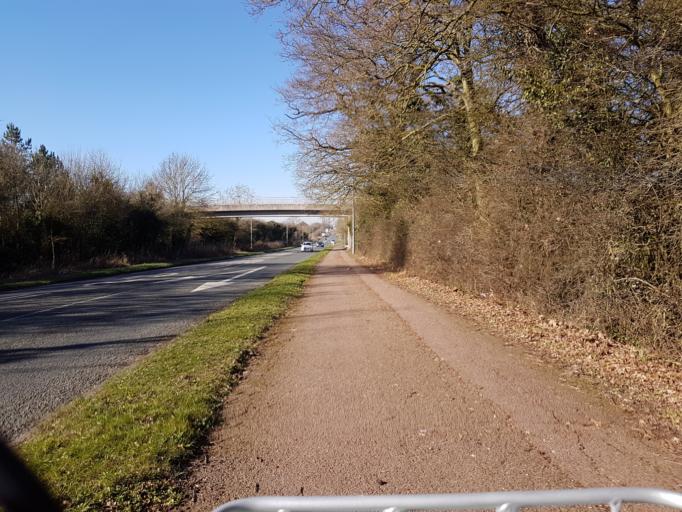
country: GB
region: England
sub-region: Milton Keynes
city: Milton Keynes
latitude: 52.0157
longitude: -0.7591
